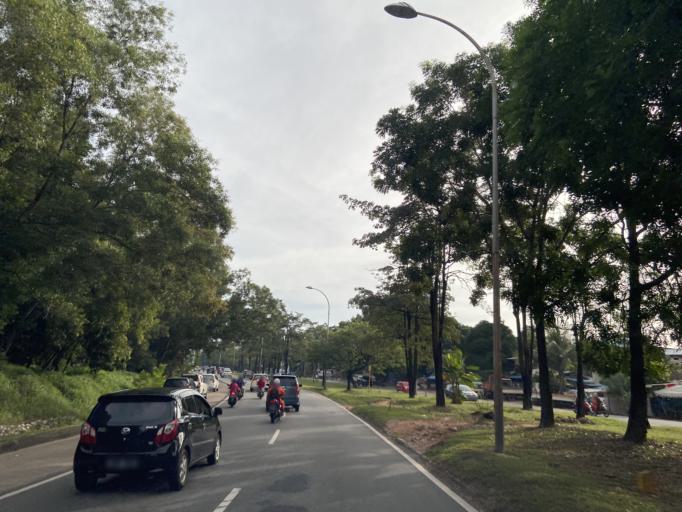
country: SG
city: Singapore
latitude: 1.1343
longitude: 104.0229
